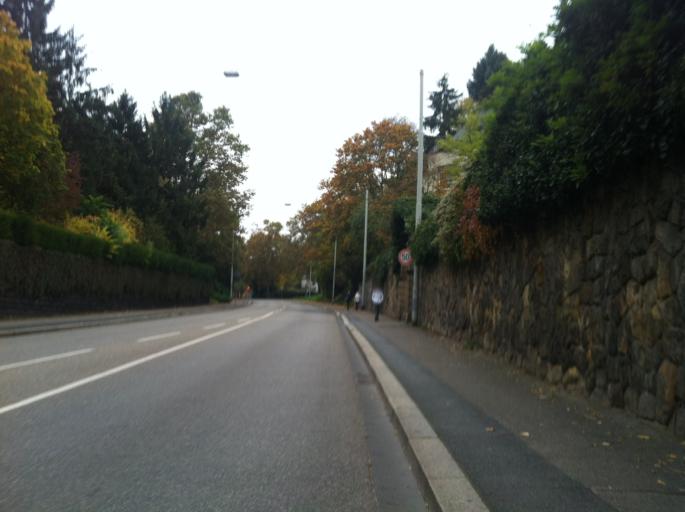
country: DE
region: Rheinland-Pfalz
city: Mainz
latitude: 49.9922
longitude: 8.2782
